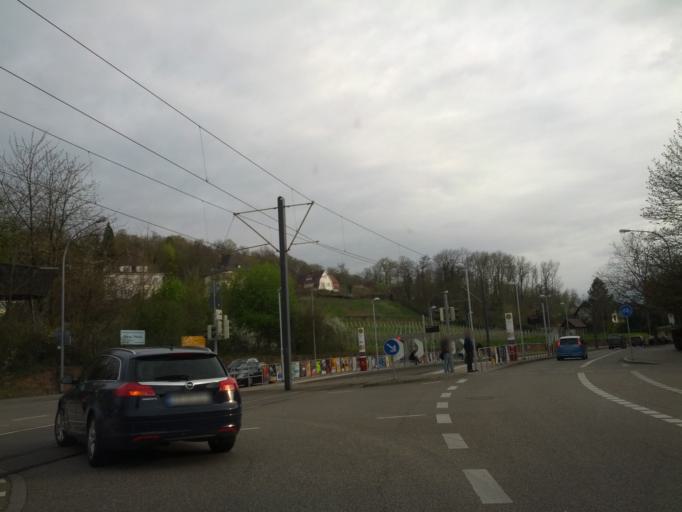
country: DE
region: Baden-Wuerttemberg
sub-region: Freiburg Region
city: Merzhausen
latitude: 47.9846
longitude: 7.8367
